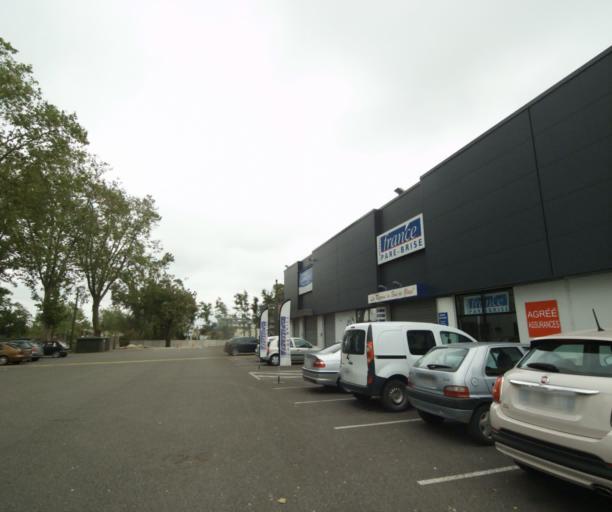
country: FR
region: Midi-Pyrenees
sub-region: Departement du Tarn-et-Garonne
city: Montauban
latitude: 43.9946
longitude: 1.3375
